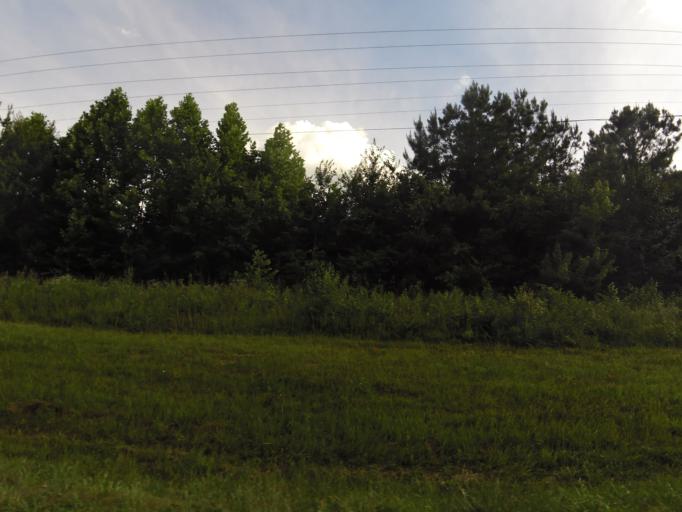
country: US
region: Tennessee
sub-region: Carroll County
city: Bruceton
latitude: 36.0370
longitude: -88.2945
